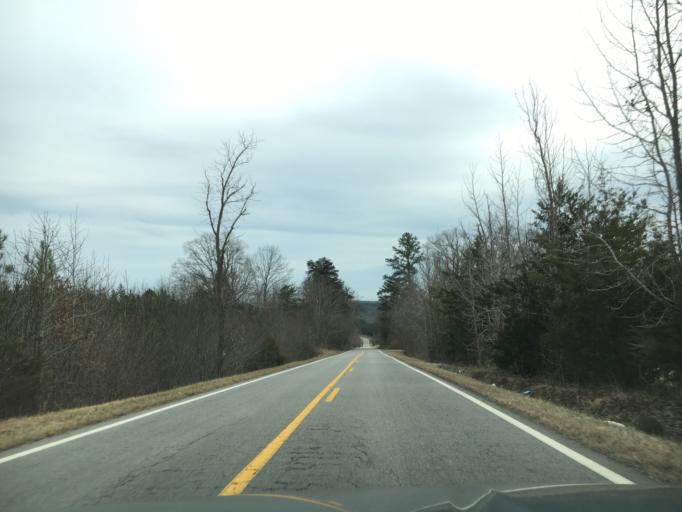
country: US
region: Virginia
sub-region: Charlotte County
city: Charlotte Court House
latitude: 37.1599
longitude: -78.7734
